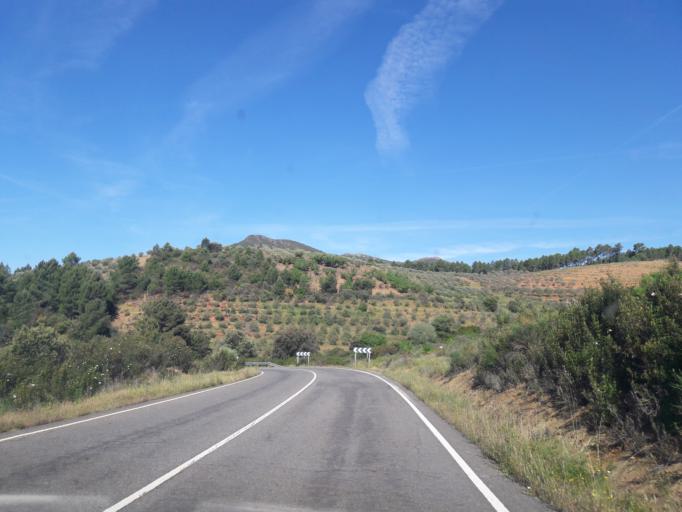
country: ES
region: Castille and Leon
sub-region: Provincia de Salamanca
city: Sotoserrano
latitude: 40.4149
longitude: -6.0391
